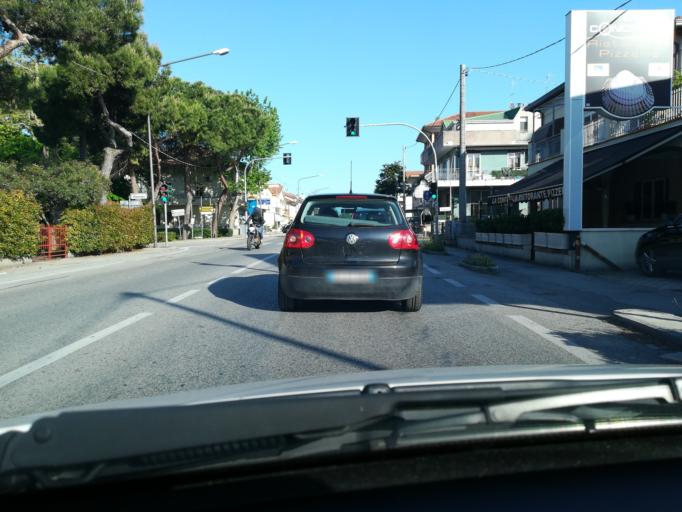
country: IT
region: Emilia-Romagna
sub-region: Provincia di Rimini
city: Riccione
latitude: 43.9890
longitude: 12.6702
